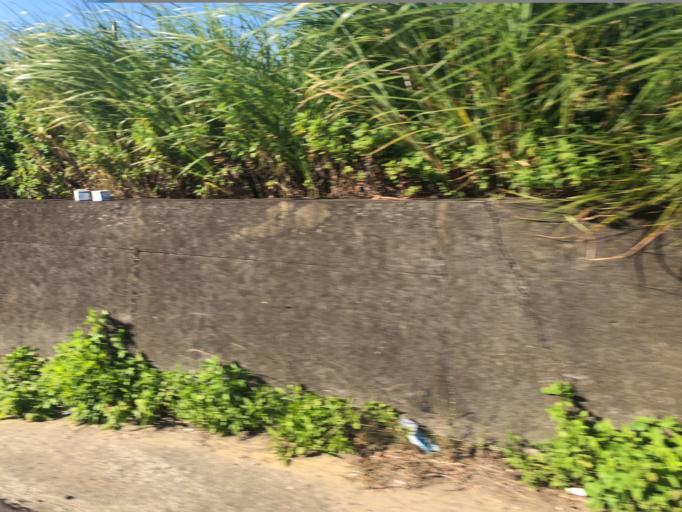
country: TW
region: Taiwan
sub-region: Hsinchu
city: Hsinchu
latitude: 24.7303
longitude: 120.9390
